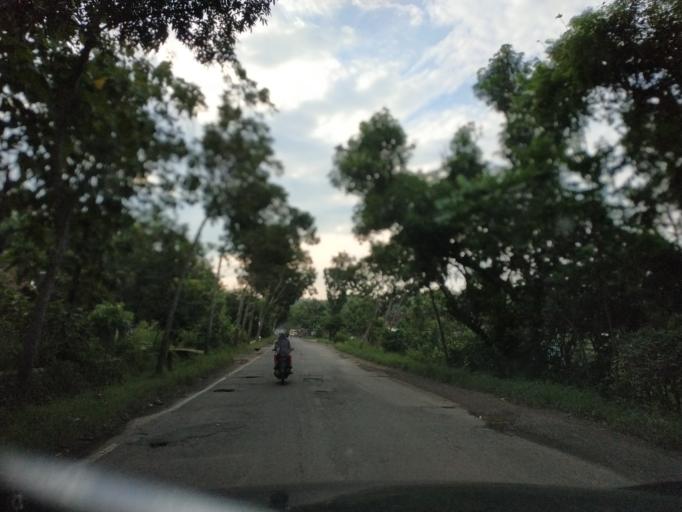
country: ID
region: Central Java
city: Ngampel
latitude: -6.9030
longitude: 111.4433
